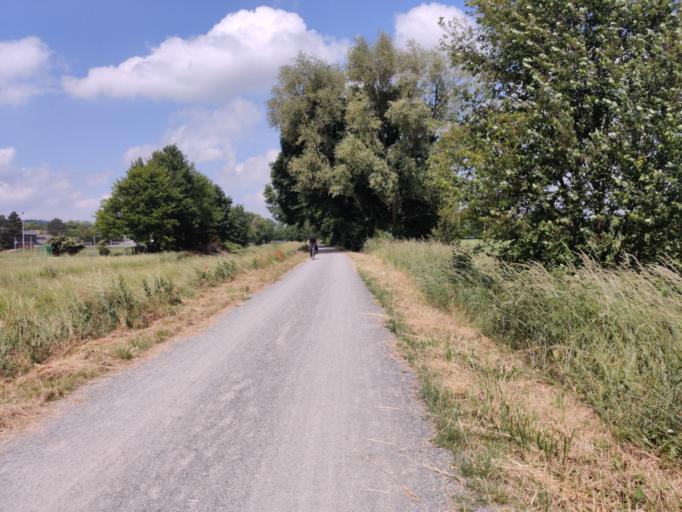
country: DE
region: Lower Saxony
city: Hildesheim
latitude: 52.1600
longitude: 9.9255
